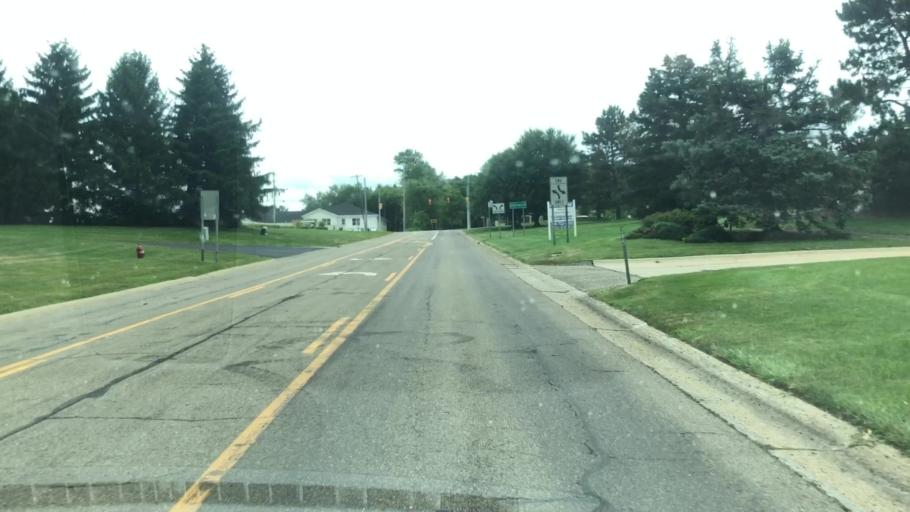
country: US
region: Ohio
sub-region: Summit County
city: Montrose-Ghent
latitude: 41.1420
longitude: -81.6392
